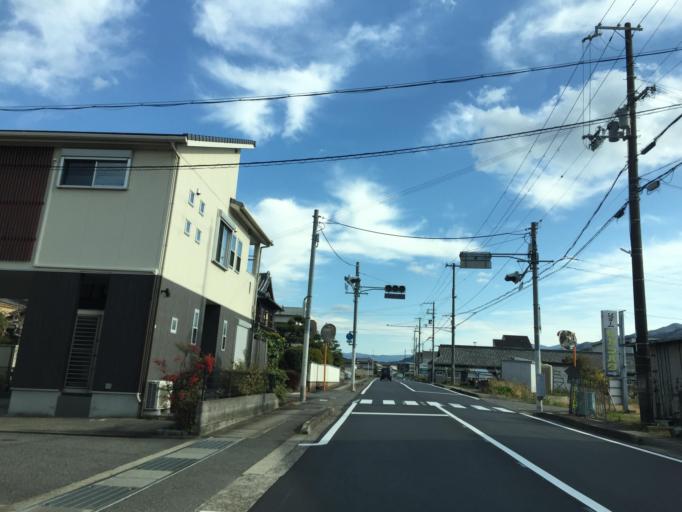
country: JP
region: Wakayama
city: Kainan
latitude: 34.1620
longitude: 135.2592
